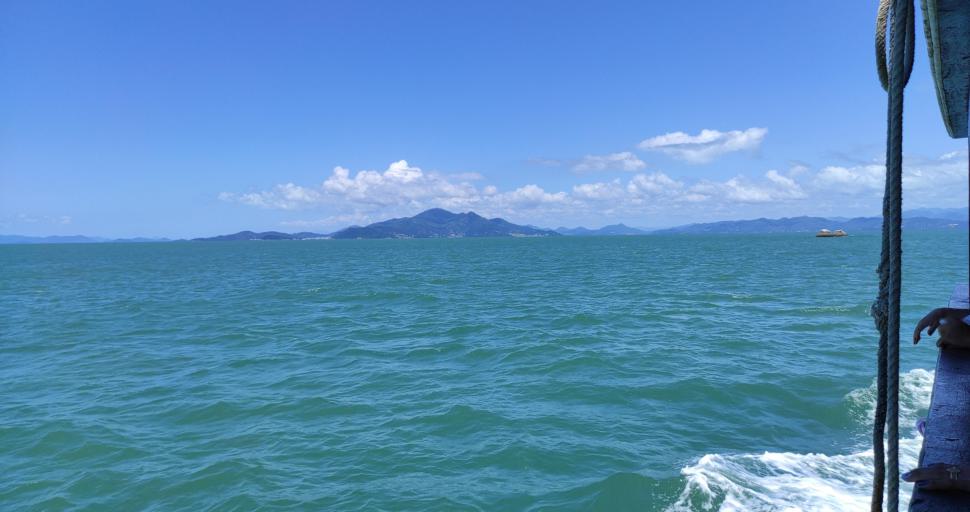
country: BR
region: Santa Catarina
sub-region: Porto Belo
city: Porto Belo
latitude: -27.2217
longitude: -48.5101
